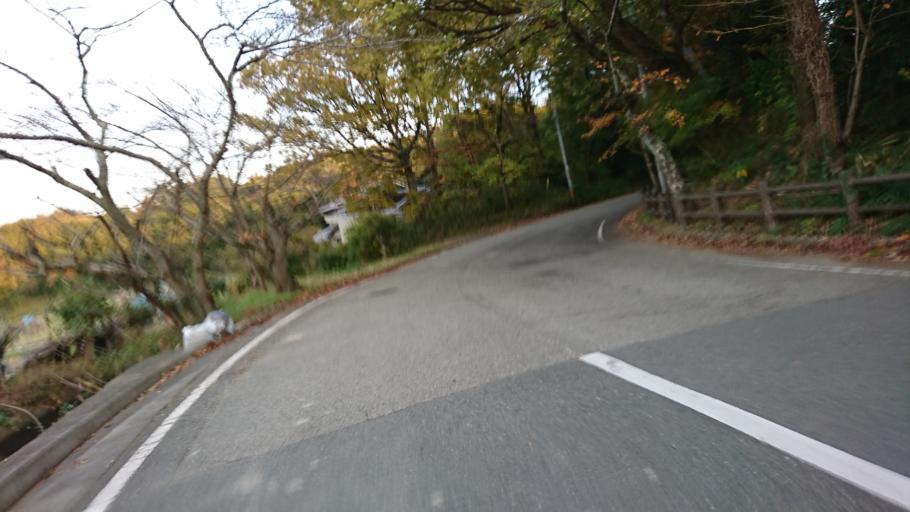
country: JP
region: Hyogo
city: Kakogawacho-honmachi
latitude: 34.7833
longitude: 134.8638
